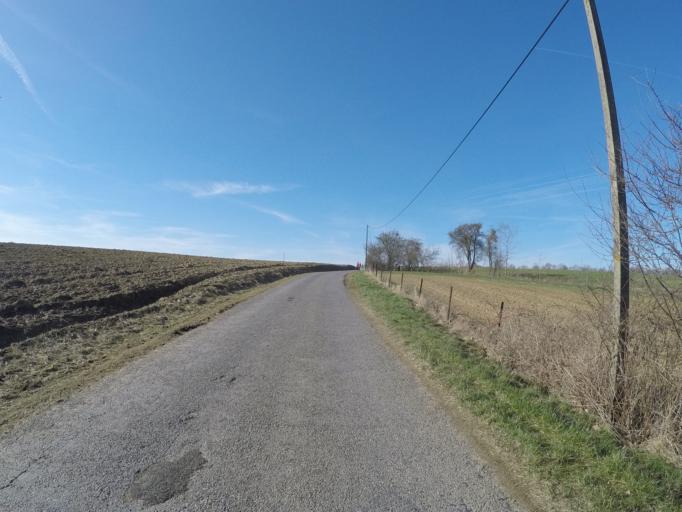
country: BE
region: Wallonia
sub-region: Province de Namur
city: Hamois
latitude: 50.3428
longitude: 5.1363
